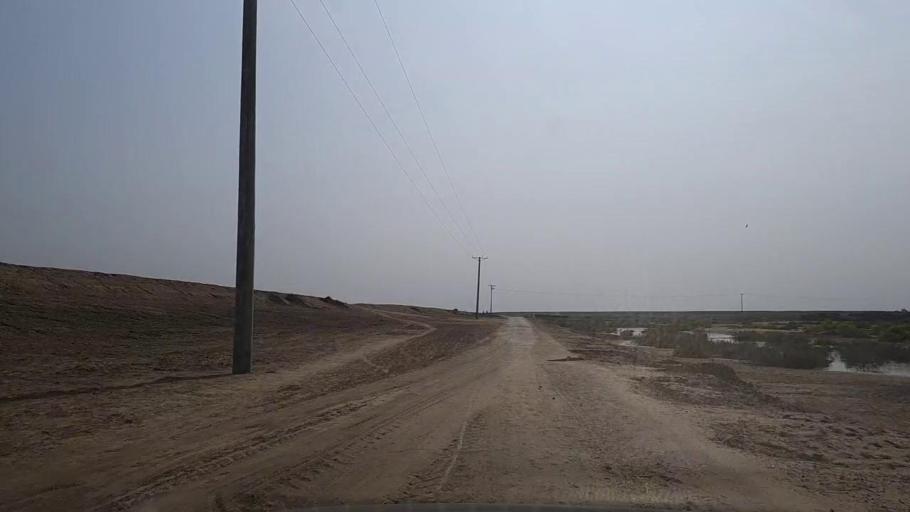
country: PK
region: Sindh
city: Thatta
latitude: 24.5762
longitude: 67.9158
